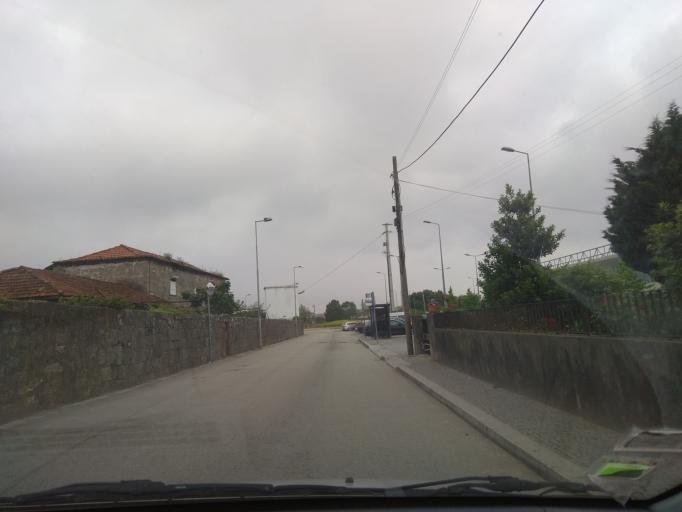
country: PT
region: Porto
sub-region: Matosinhos
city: Guifoes
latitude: 41.1997
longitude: -8.6657
